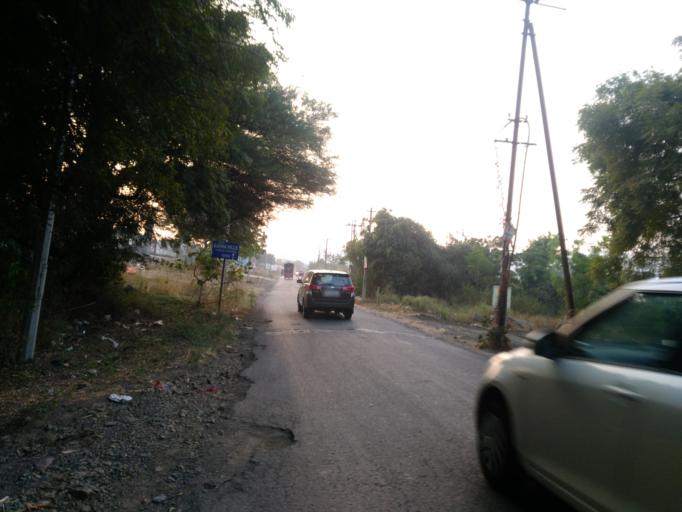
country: IN
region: Maharashtra
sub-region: Pune Division
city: Pune
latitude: 18.4283
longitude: 73.8998
